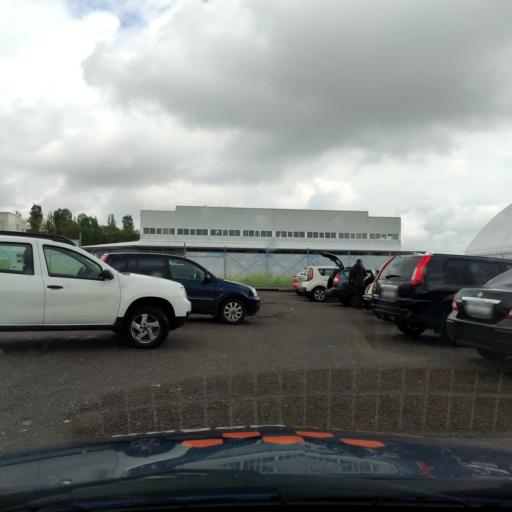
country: RU
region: Voronezj
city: Voronezh
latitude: 51.6413
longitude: 39.1382
